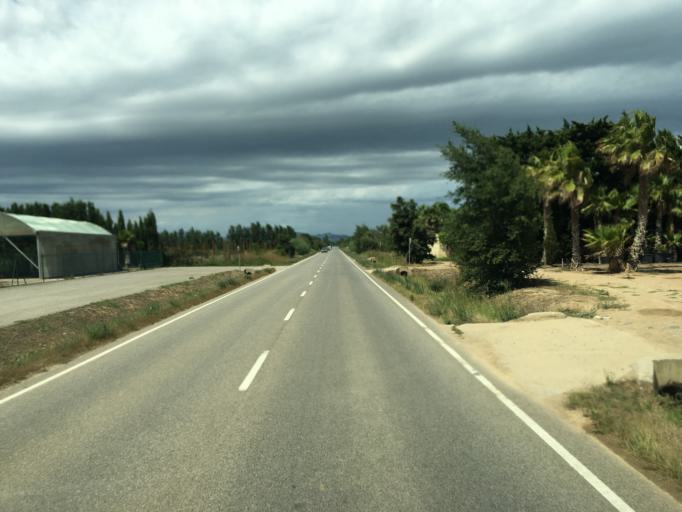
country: ES
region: Catalonia
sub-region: Provincia de Girona
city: Sant Pere Pescador
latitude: 42.2016
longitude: 3.0840
